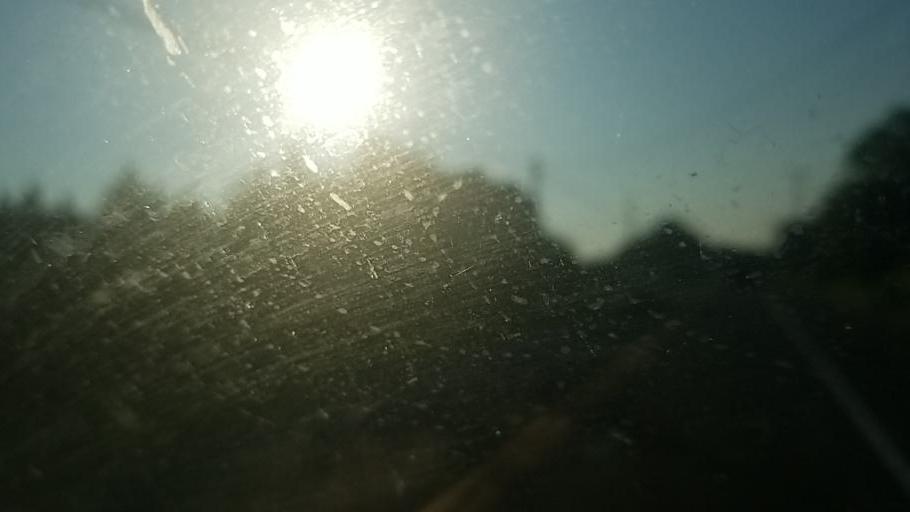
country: US
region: Maryland
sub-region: Worcester County
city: Ocean Pines
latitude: 38.4608
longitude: -75.1367
